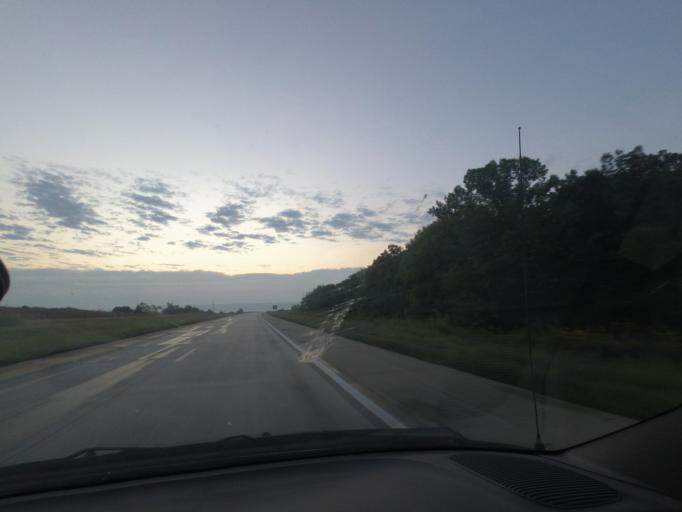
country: US
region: Missouri
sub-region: Macon County
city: Macon
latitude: 39.7585
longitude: -92.6473
